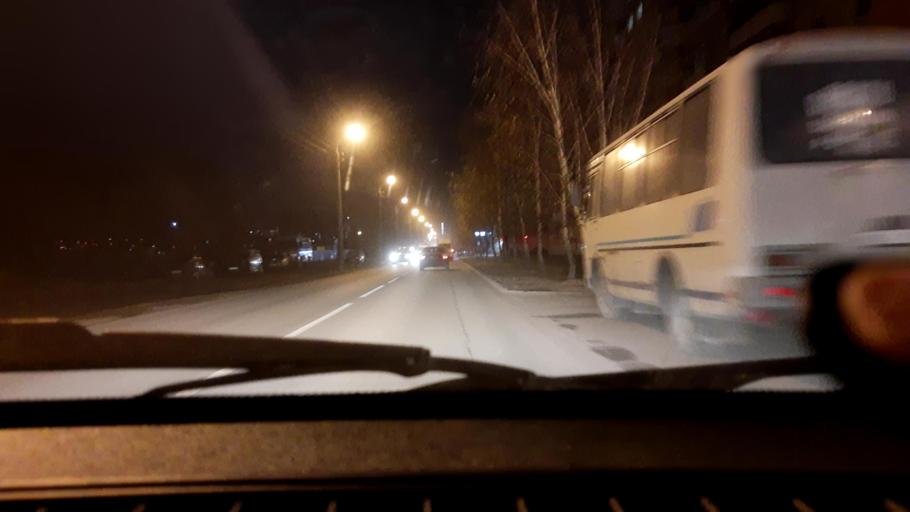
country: RU
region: Bashkortostan
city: Mikhaylovka
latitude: 54.7099
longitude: 55.8370
